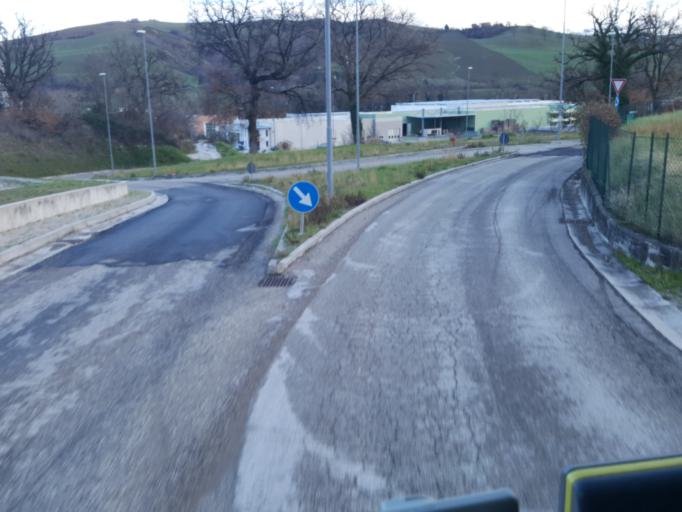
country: IT
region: The Marches
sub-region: Provincia di Macerata
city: San Severino Marche
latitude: 43.2489
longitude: 13.2281
